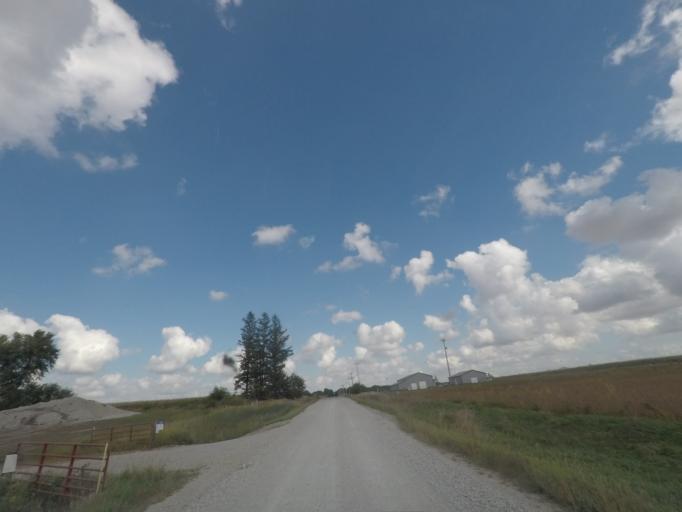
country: US
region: Iowa
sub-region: Story County
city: Nevada
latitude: 42.0036
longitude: -93.3191
